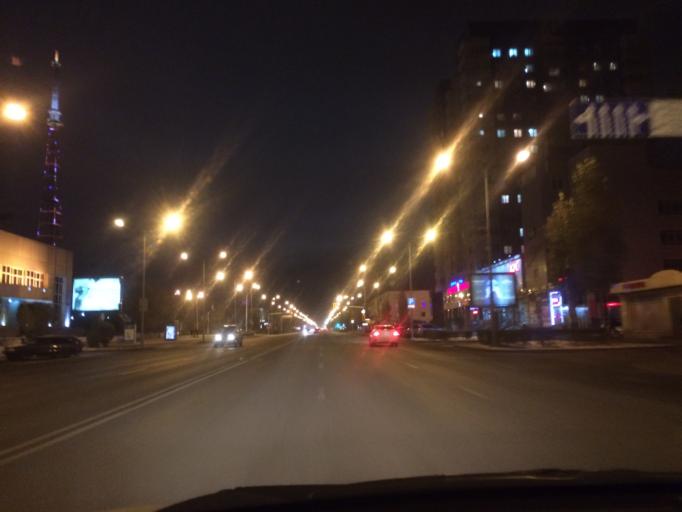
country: KZ
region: Astana Qalasy
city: Astana
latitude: 51.1867
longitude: 71.4079
